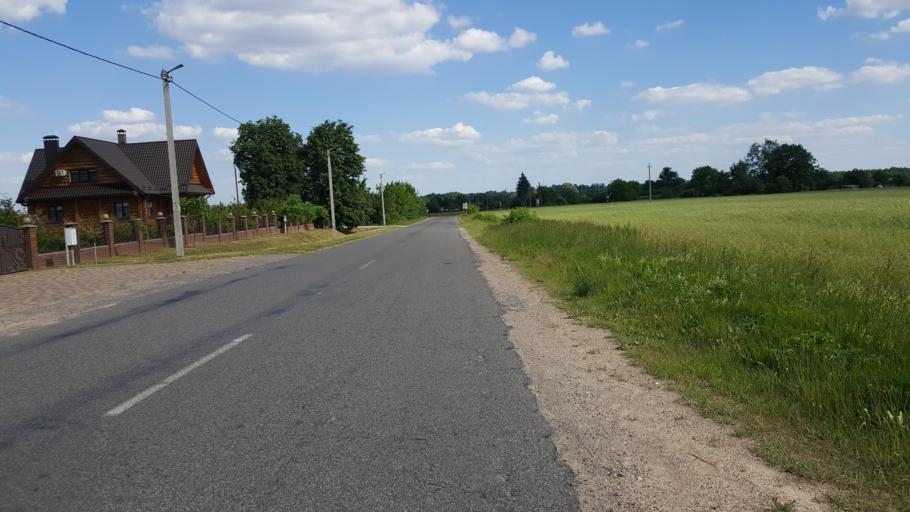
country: BY
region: Brest
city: Kamyanyets
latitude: 52.4088
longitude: 23.7939
